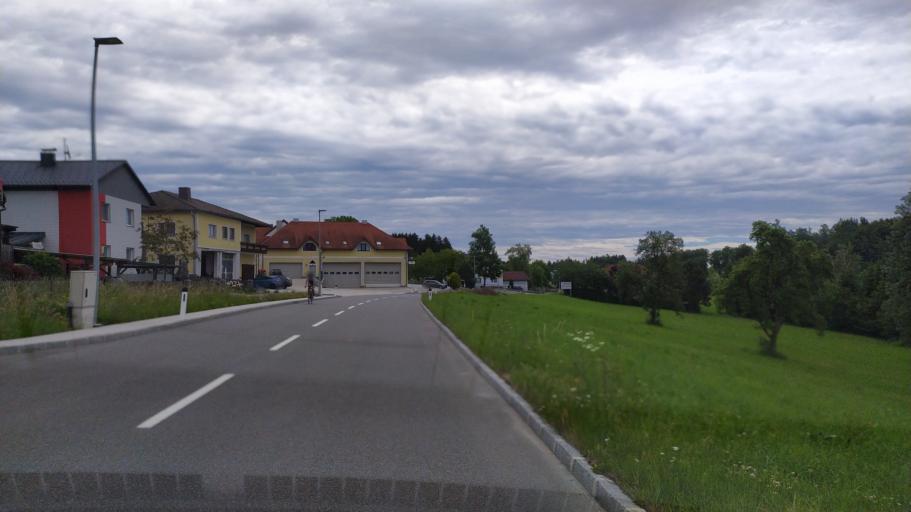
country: AT
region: Upper Austria
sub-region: Politischer Bezirk Perg
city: Perg
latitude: 48.2605
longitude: 14.6538
